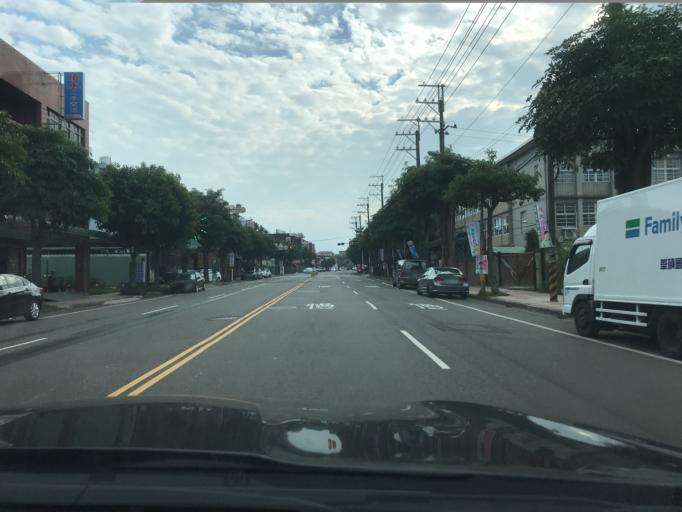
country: TW
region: Taiwan
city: Daxi
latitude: 24.9101
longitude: 121.2795
